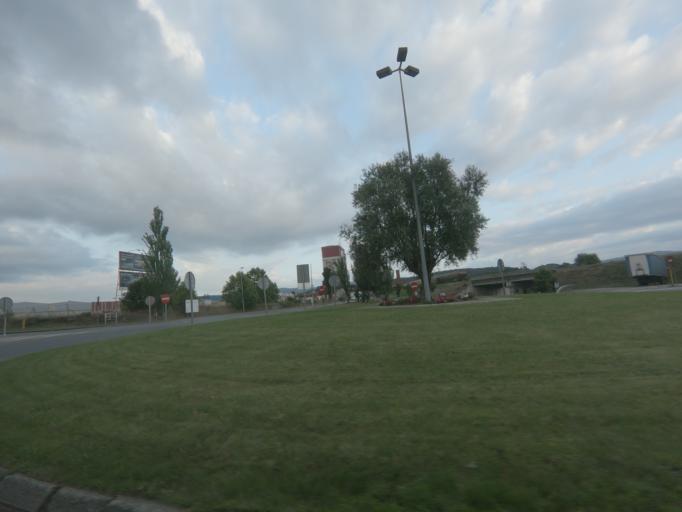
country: ES
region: Galicia
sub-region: Provincia de Ourense
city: Taboadela
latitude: 42.2881
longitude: -7.8278
